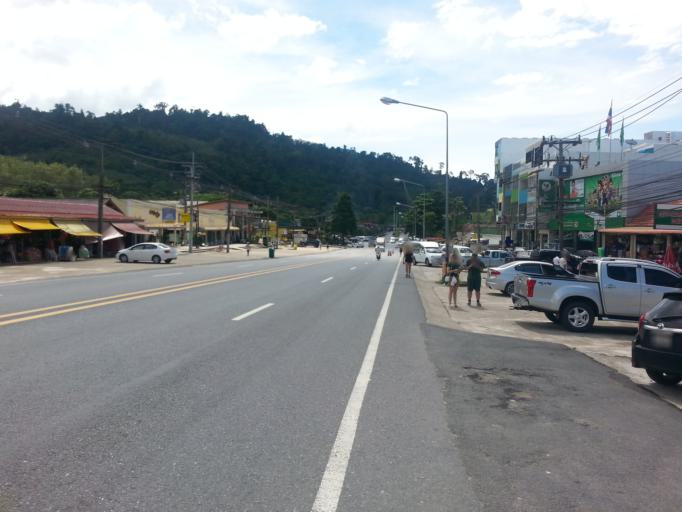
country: TH
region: Phangnga
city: Ban Khao Lak
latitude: 8.6466
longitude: 98.2518
